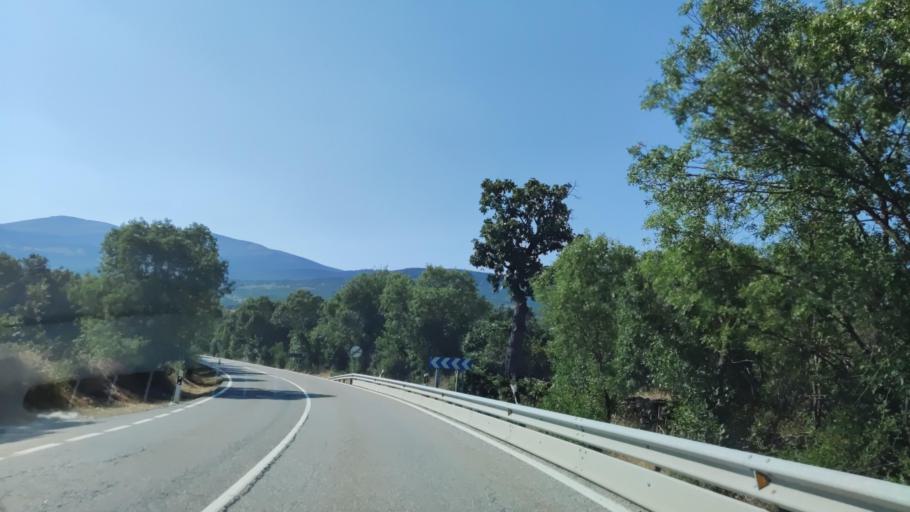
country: ES
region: Madrid
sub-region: Provincia de Madrid
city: Lozoya
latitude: 40.9542
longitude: -3.7749
